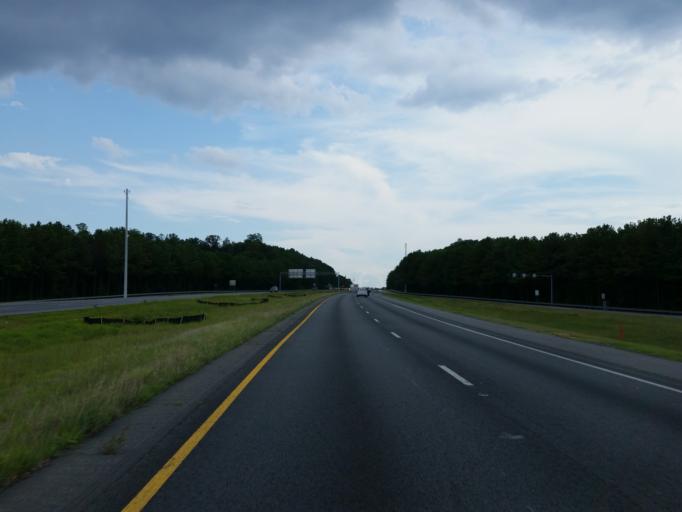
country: US
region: Georgia
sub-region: Cobb County
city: Kennesaw
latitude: 34.0120
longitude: -84.5591
